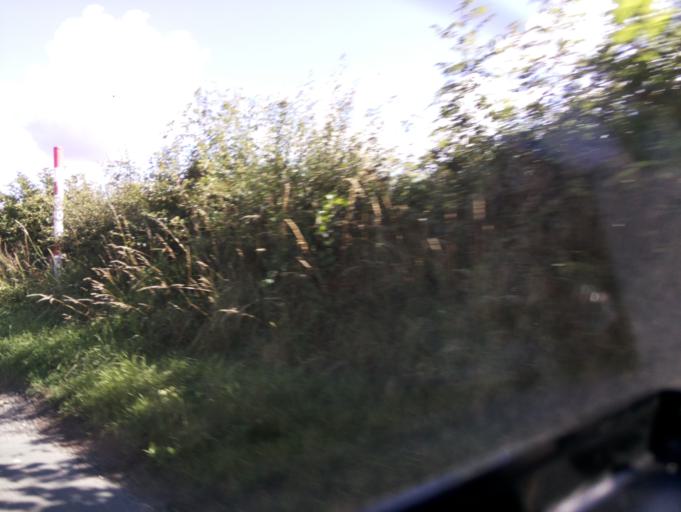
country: GB
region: England
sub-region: Herefordshire
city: Yatton
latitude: 51.9463
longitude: -2.5315
